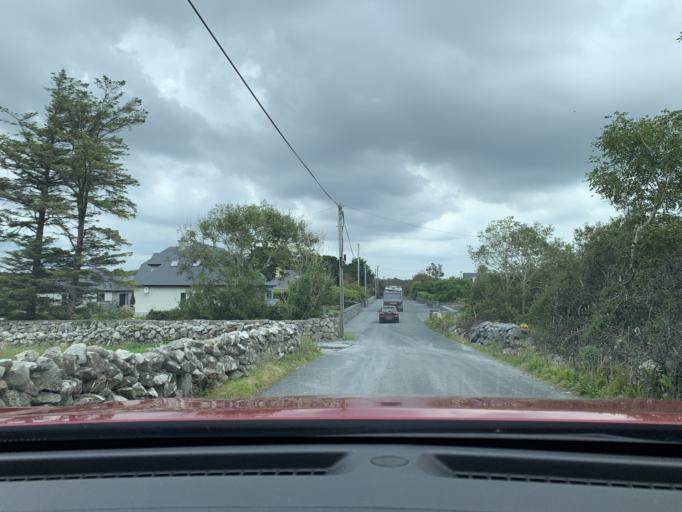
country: IE
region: Connaught
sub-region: County Galway
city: Bearna
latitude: 53.2789
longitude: -9.1168
